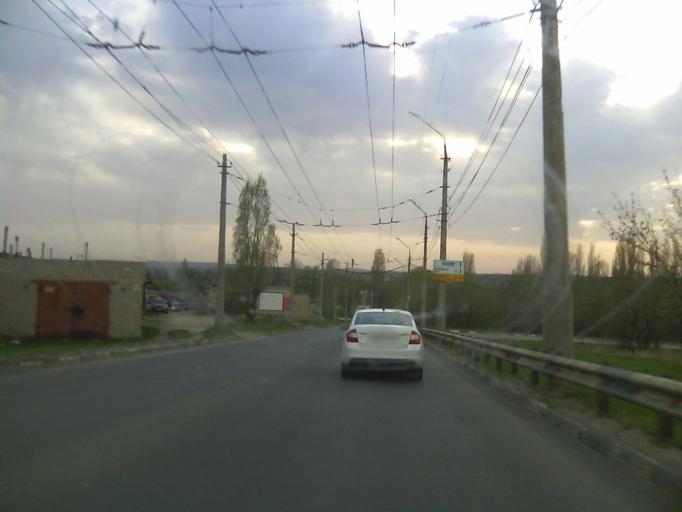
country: RU
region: Saratov
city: Sokolovyy
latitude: 51.5913
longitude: 45.9060
